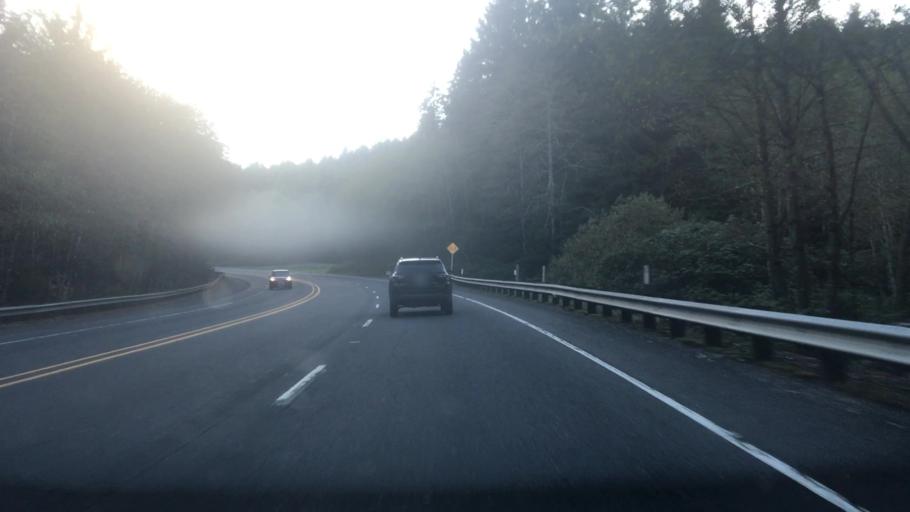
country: US
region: Oregon
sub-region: Clatsop County
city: Cannon Beach
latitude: 45.9208
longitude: -123.9367
